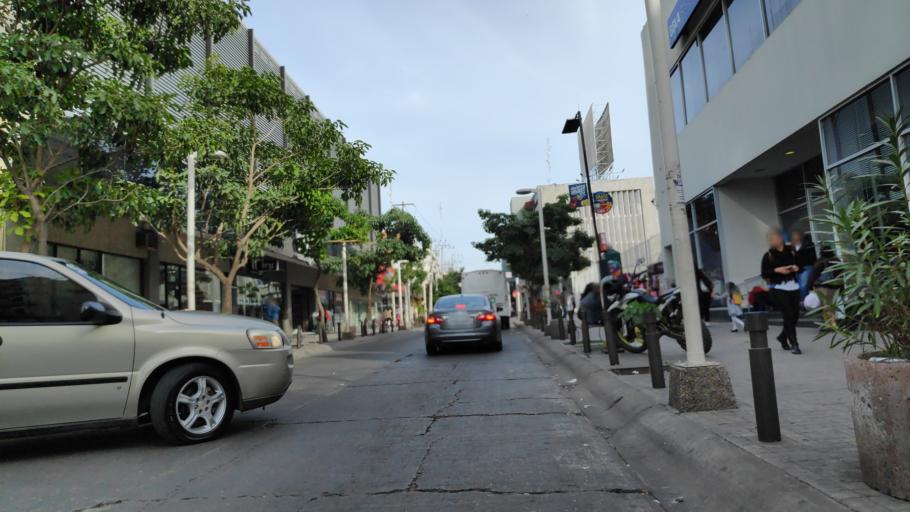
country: MX
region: Sinaloa
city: Culiacan
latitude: 24.8098
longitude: -107.3958
